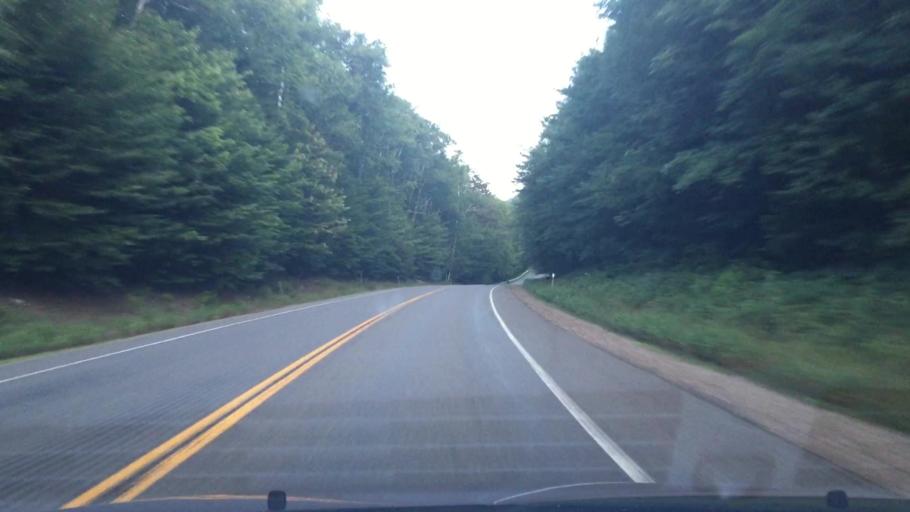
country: US
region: New Hampshire
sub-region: Grafton County
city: Woodstock
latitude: 44.0506
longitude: -71.5667
